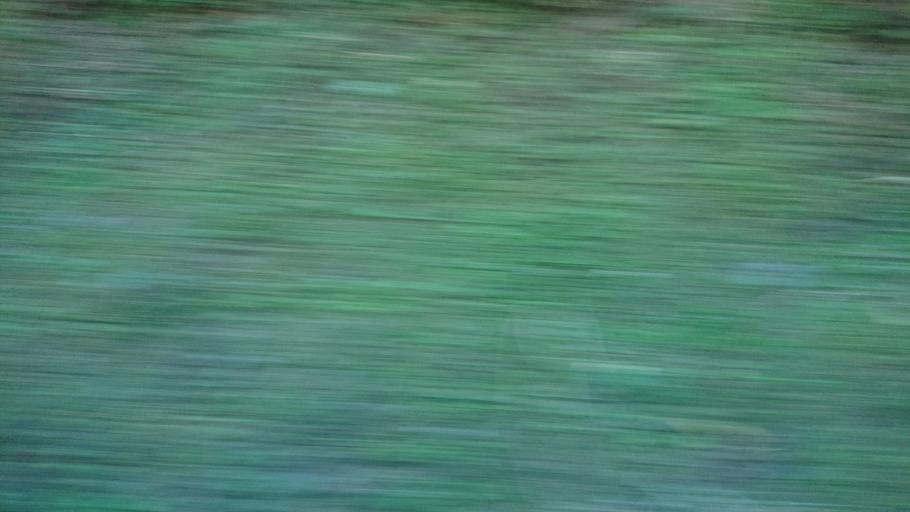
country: TW
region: Taiwan
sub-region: Yilan
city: Yilan
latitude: 24.5785
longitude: 121.4875
